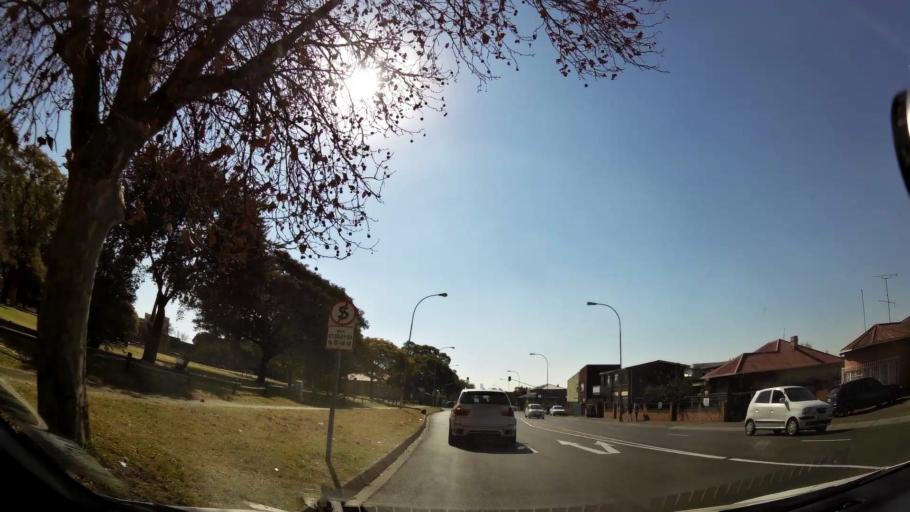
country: ZA
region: Gauteng
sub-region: City of Johannesburg Metropolitan Municipality
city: Johannesburg
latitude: -26.2495
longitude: 28.0552
